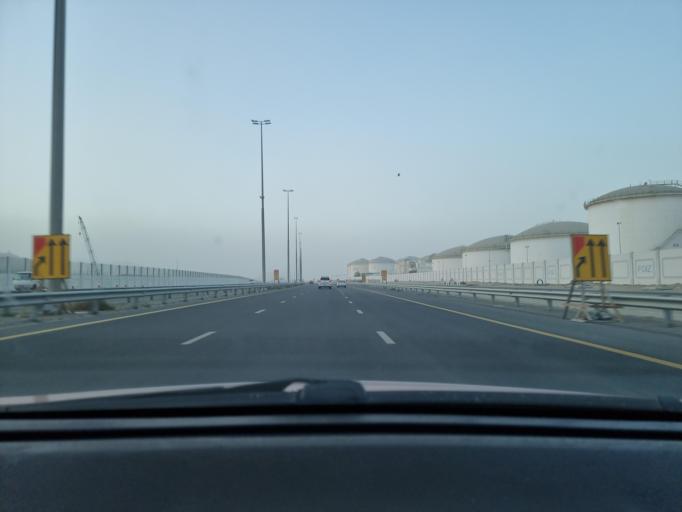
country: AE
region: Al Fujayrah
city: Al Fujayrah
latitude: 25.2090
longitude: 56.3544
